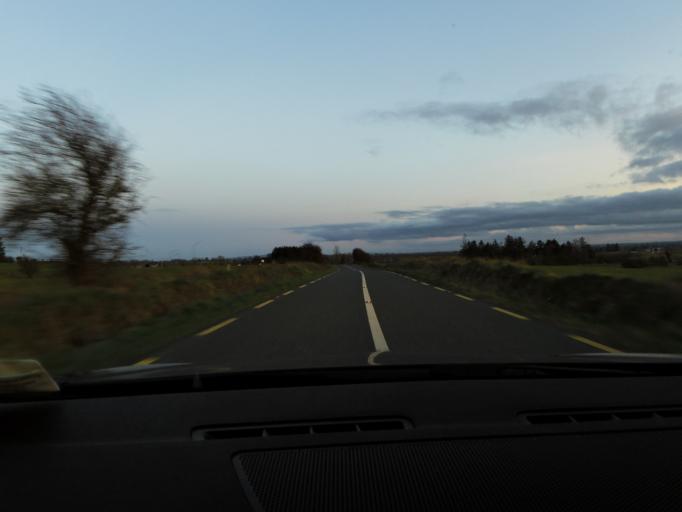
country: IE
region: Connaught
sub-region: Roscommon
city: Boyle
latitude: 53.8686
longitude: -8.2431
